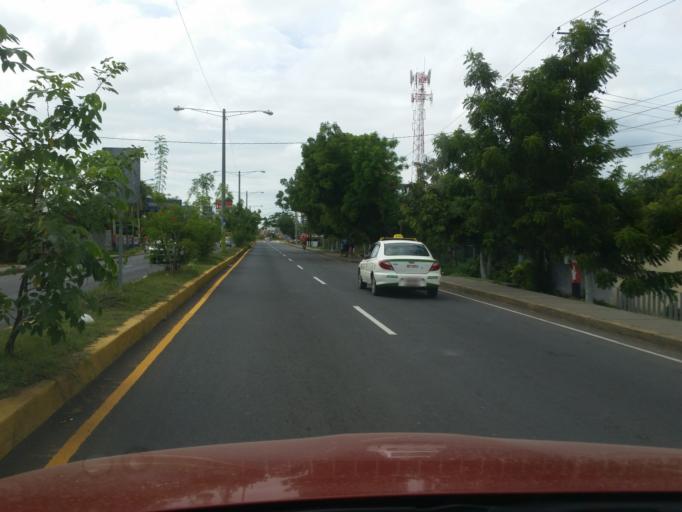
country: NI
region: Masaya
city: Masaya
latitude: 11.9898
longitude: -86.0990
